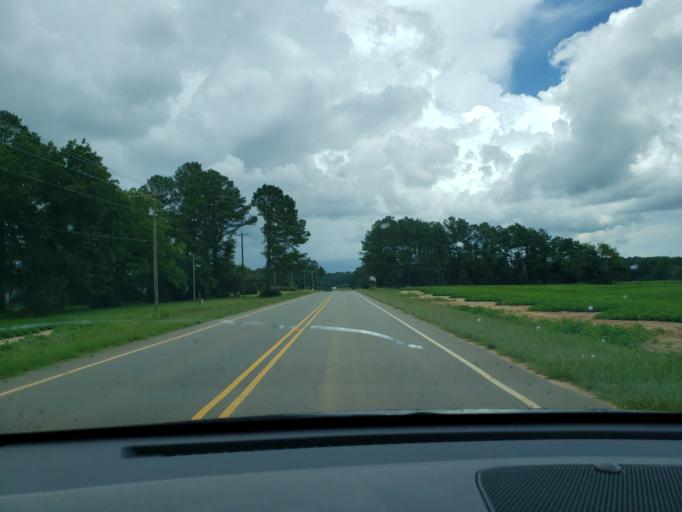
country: US
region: North Carolina
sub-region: Columbus County
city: Whiteville
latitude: 34.4632
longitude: -78.6766
